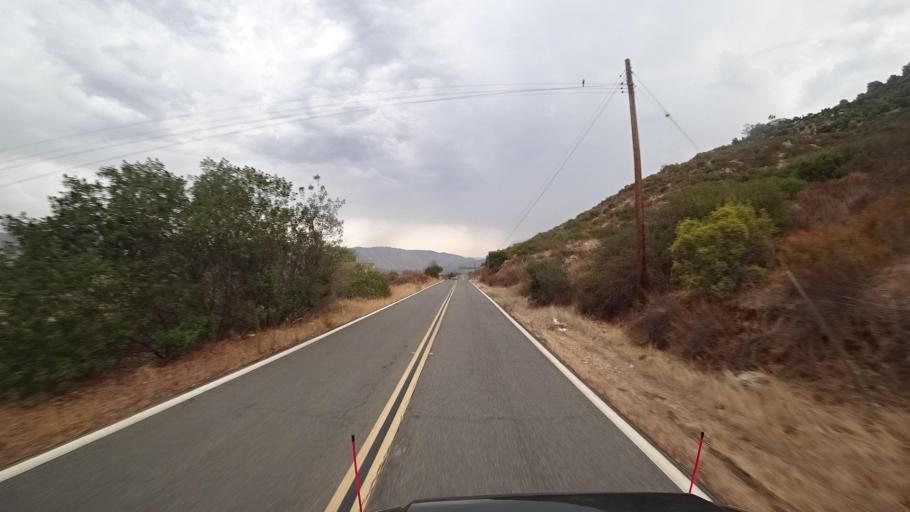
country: US
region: California
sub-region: San Diego County
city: San Pasqual
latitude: 33.0750
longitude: -116.9978
